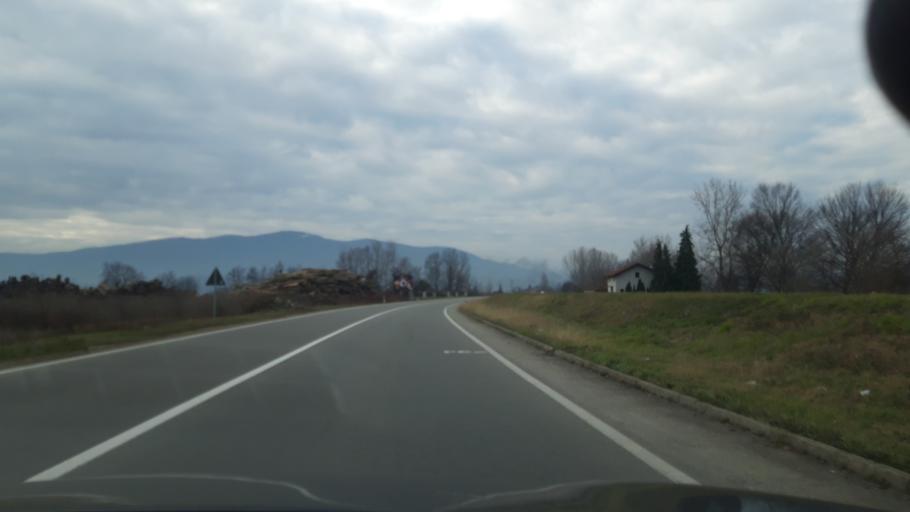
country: RS
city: Lipnicki Sor
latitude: 44.5515
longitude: 19.1977
